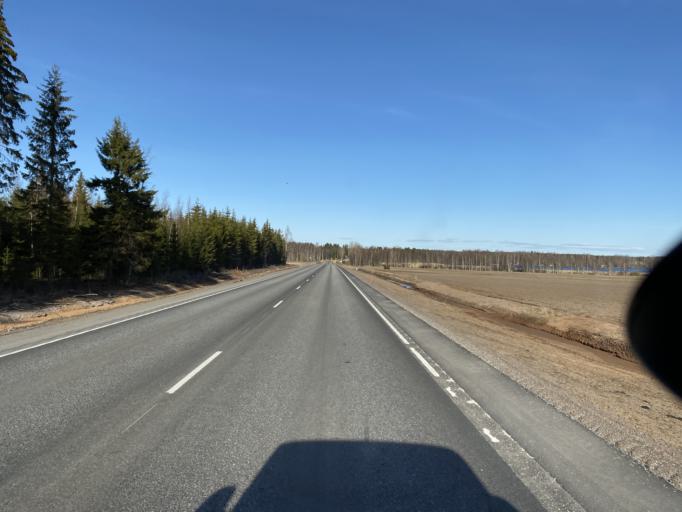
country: FI
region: Satakunta
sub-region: Rauma
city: Koeylioe
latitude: 61.1593
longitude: 22.2948
